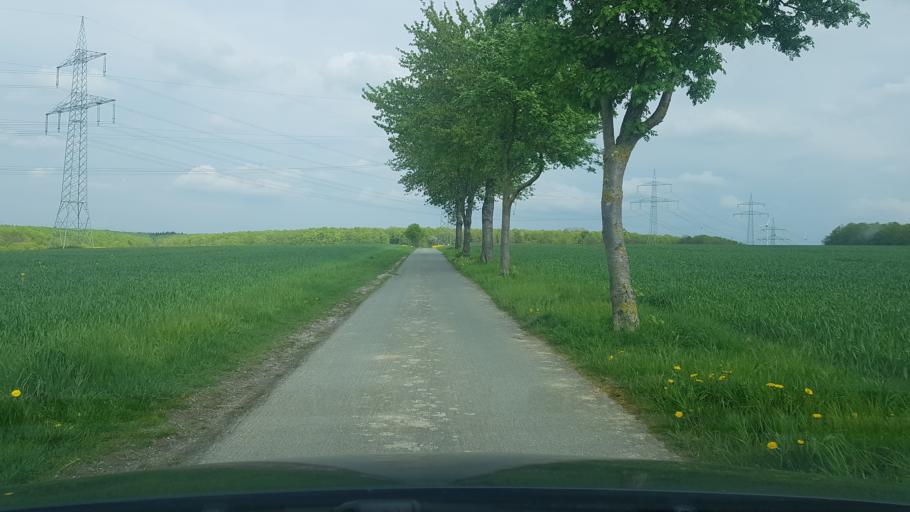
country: DE
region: North Rhine-Westphalia
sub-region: Regierungsbezirk Detmold
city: Paderborn
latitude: 51.6512
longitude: 8.7645
